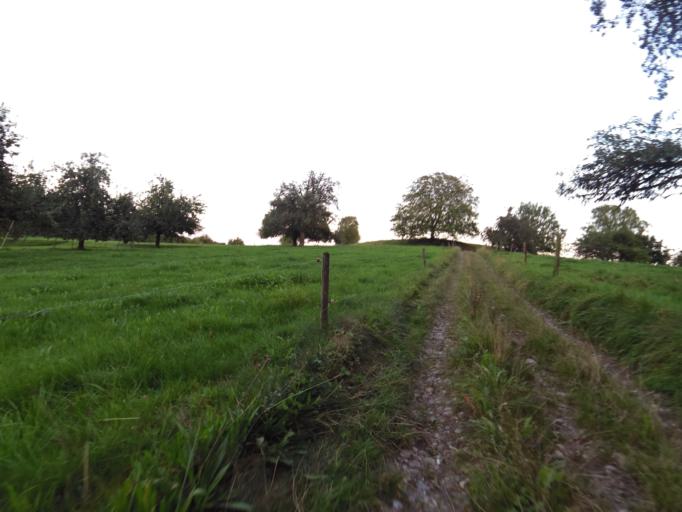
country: CH
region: Thurgau
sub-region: Weinfelden District
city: Wigoltingen
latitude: 47.5723
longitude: 9.0131
